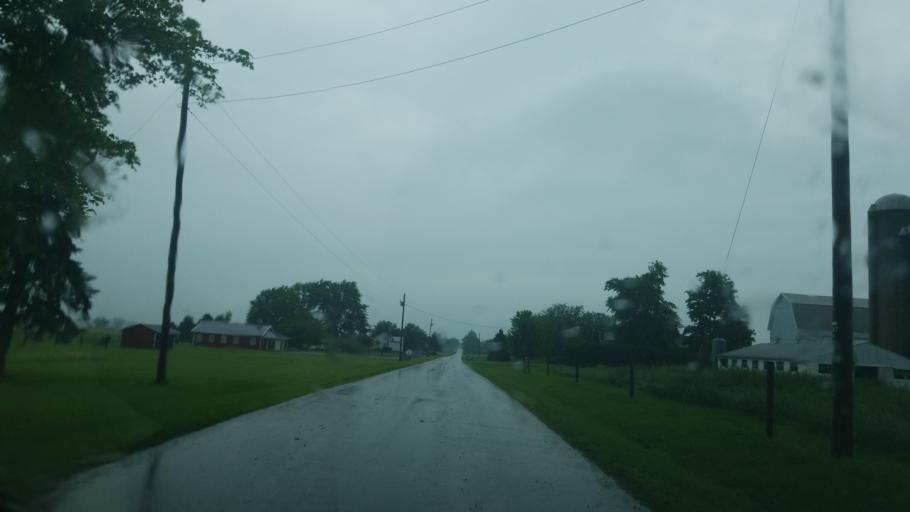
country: US
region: Ohio
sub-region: Huron County
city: Greenwich
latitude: 41.0574
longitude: -82.5854
